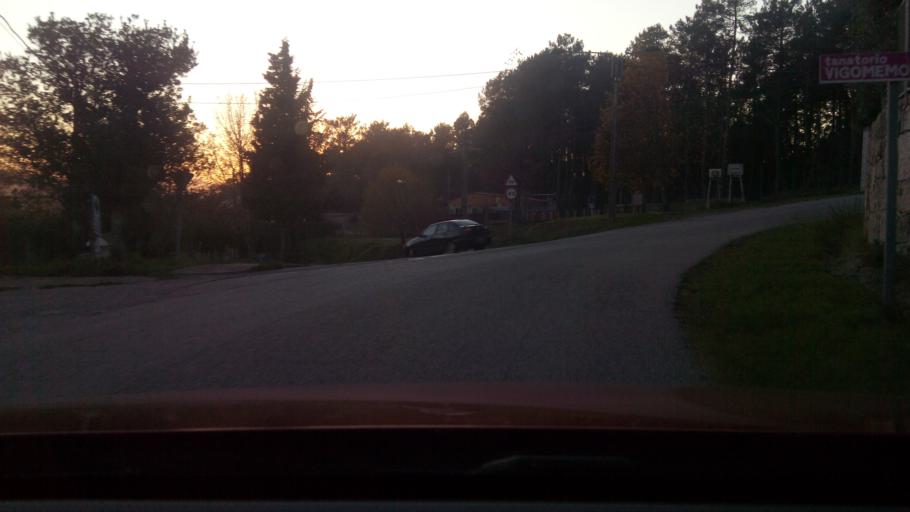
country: ES
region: Galicia
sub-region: Provincia de Pontevedra
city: Porrino
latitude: 42.1664
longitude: -8.6914
